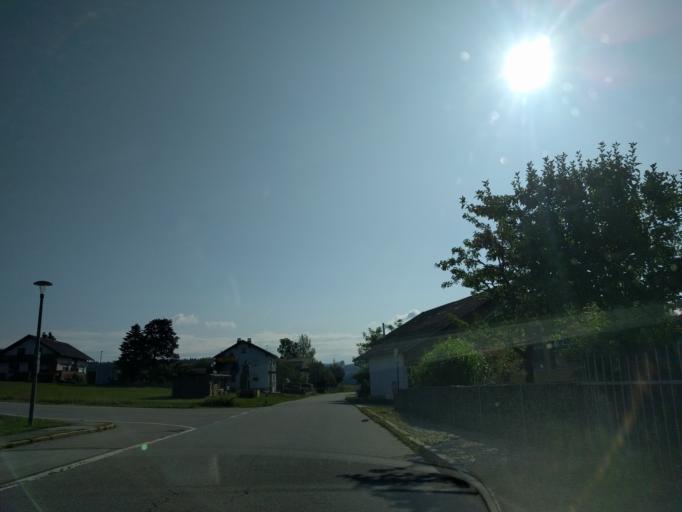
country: DE
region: Bavaria
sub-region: Lower Bavaria
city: Mauth
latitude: 48.8663
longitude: 13.5467
